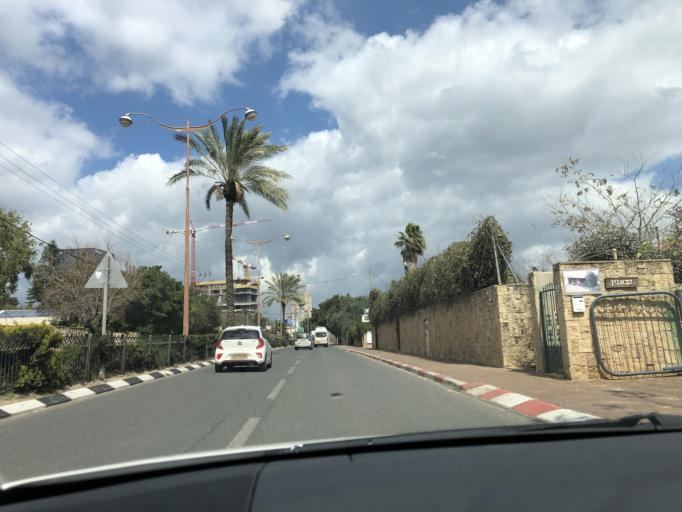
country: IL
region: Central District
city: Hod HaSharon
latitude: 32.1693
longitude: 34.8937
